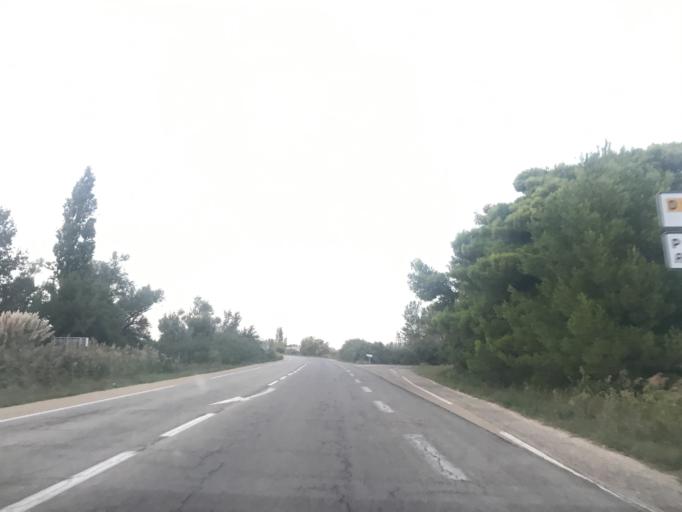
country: FR
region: Provence-Alpes-Cote d'Azur
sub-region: Departement des Bouches-du-Rhone
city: Saintes-Maries-de-la-Mer
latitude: 43.5197
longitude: 4.3992
